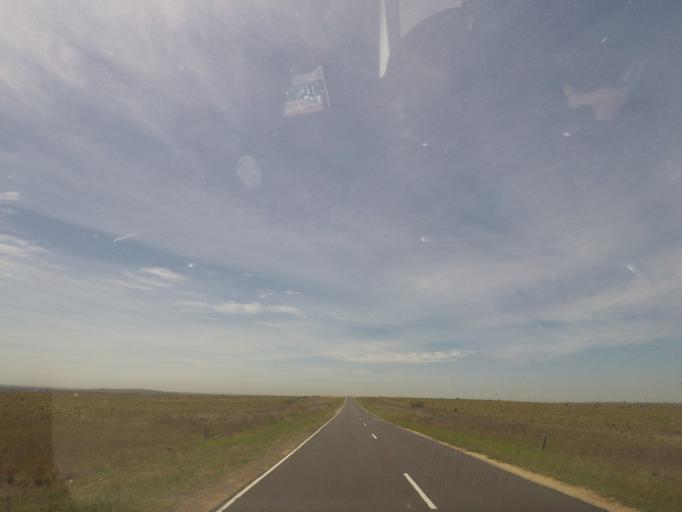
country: AU
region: Victoria
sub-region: Wyndham
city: Wyndham Vale
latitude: -37.7964
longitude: 144.4825
